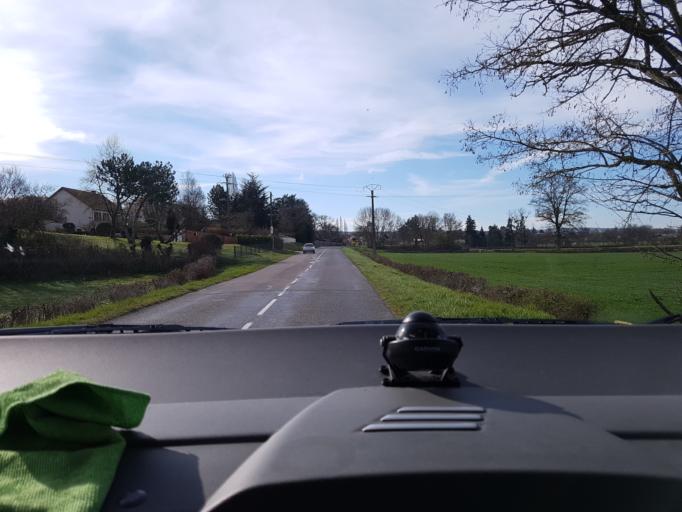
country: FR
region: Bourgogne
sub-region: Departement de Saone-et-Loire
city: Toulon-sur-Arroux
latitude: 46.7026
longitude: 4.1375
